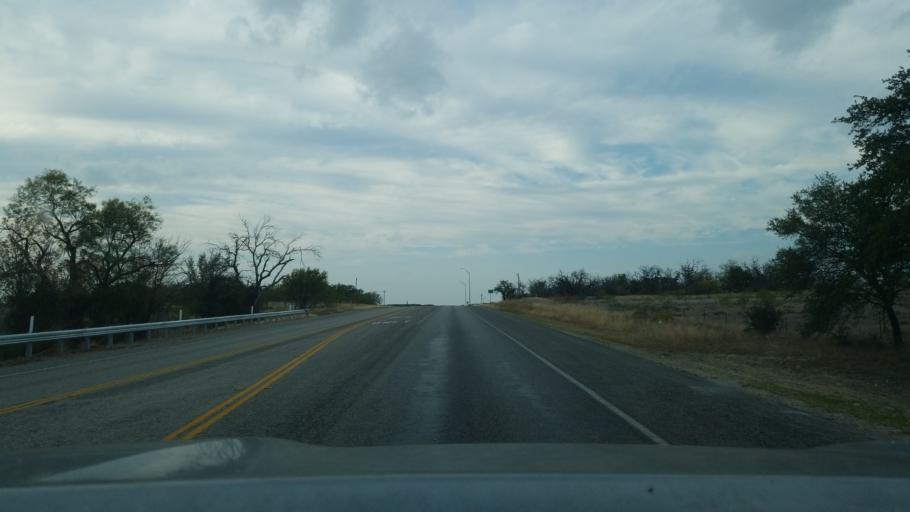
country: US
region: Texas
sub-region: Mills County
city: Goldthwaite
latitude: 31.5190
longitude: -98.5936
